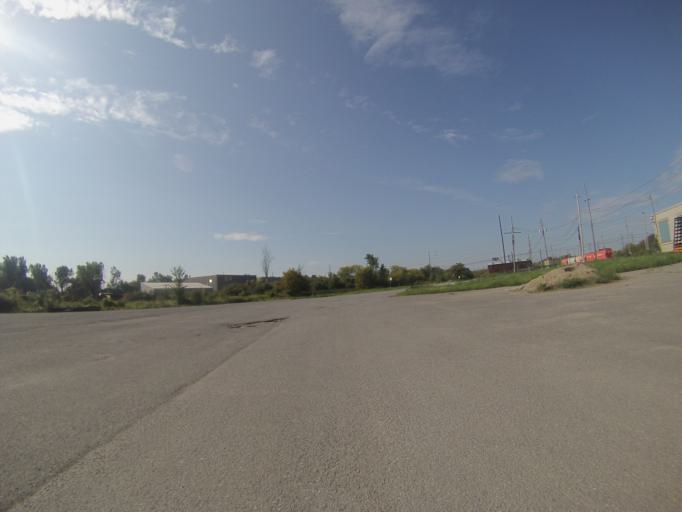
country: CA
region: Ontario
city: Ottawa
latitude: 45.3666
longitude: -75.6481
